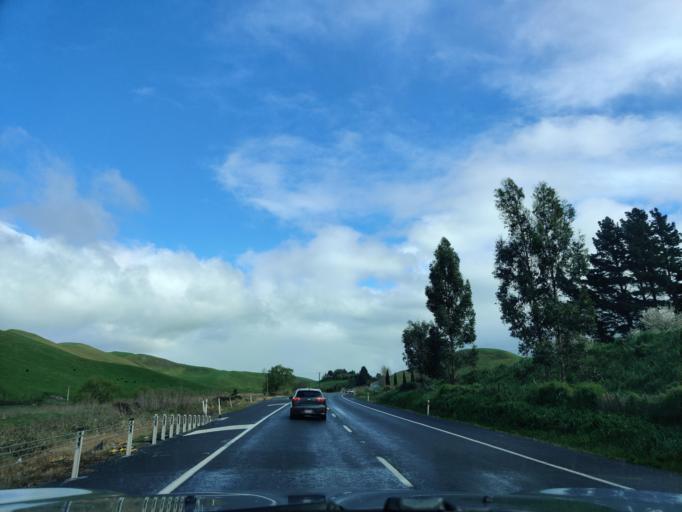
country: NZ
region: Hawke's Bay
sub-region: Hastings District
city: Hastings
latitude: -39.7127
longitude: 176.7834
